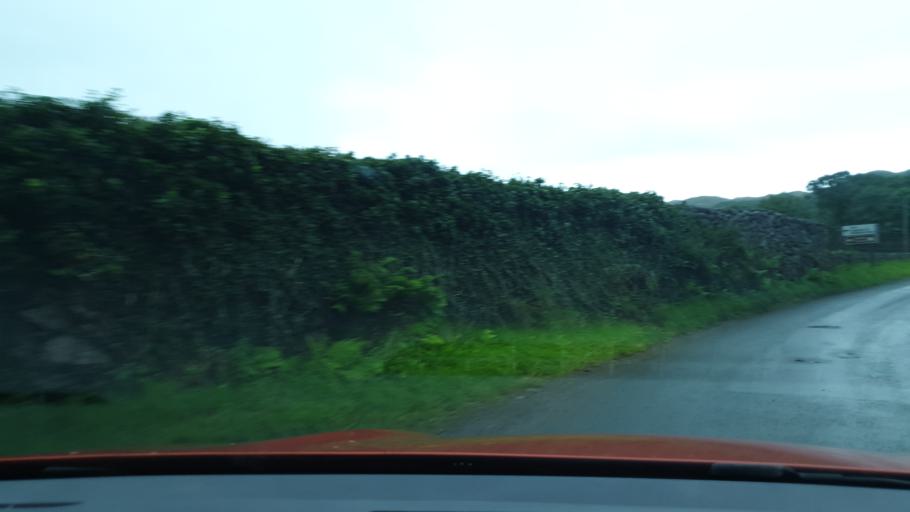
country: GB
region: England
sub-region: Cumbria
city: Seascale
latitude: 54.3872
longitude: -3.3131
